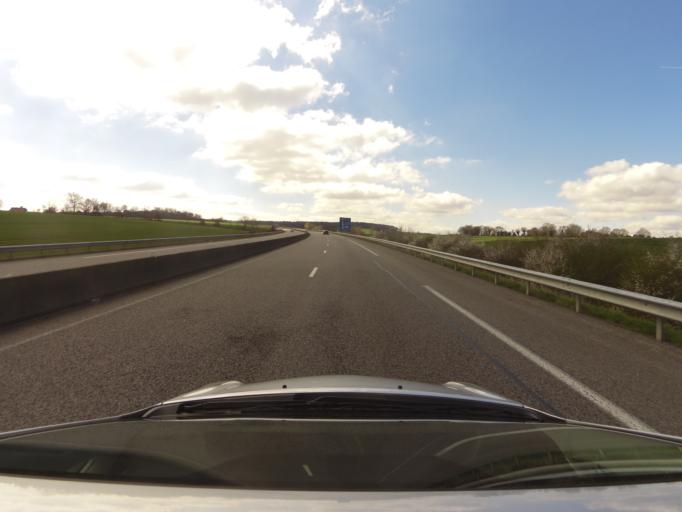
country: FR
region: Haute-Normandie
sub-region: Departement de la Seine-Maritime
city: Neufchatel-en-Bray
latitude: 49.7789
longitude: 1.4746
